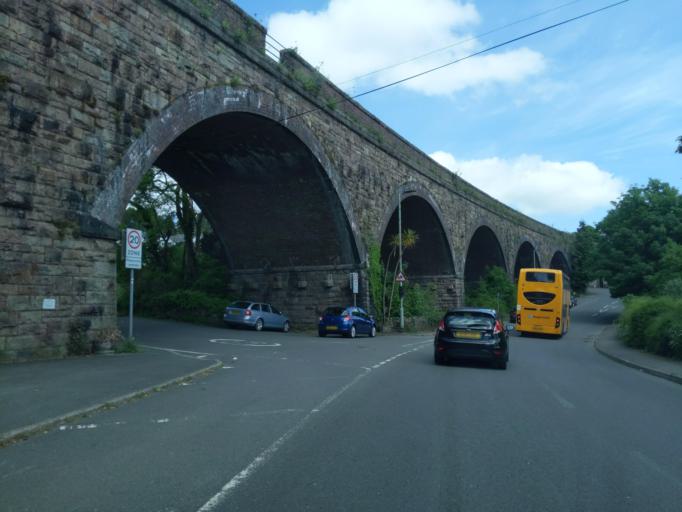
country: GB
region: England
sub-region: Devon
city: Ivybridge
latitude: 50.3971
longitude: -3.8794
